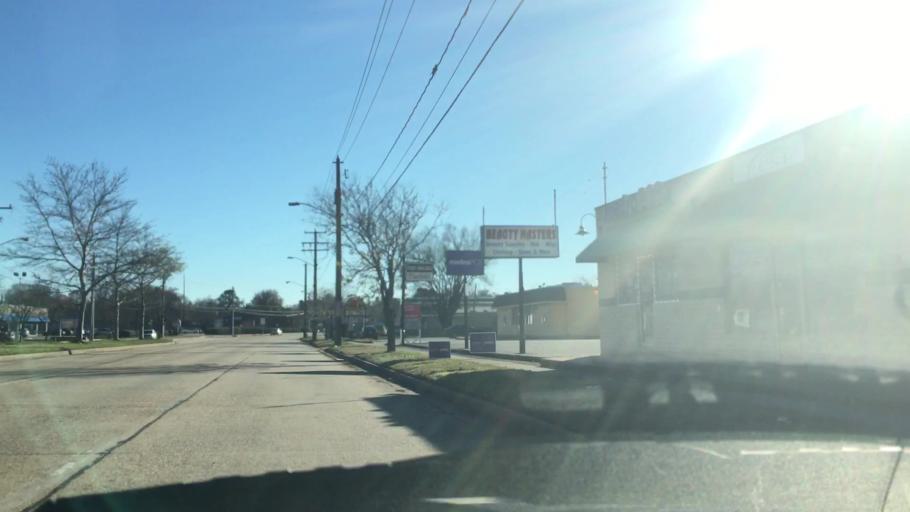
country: US
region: Virginia
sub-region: City of Norfolk
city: Norfolk
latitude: 36.8928
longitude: -76.2381
